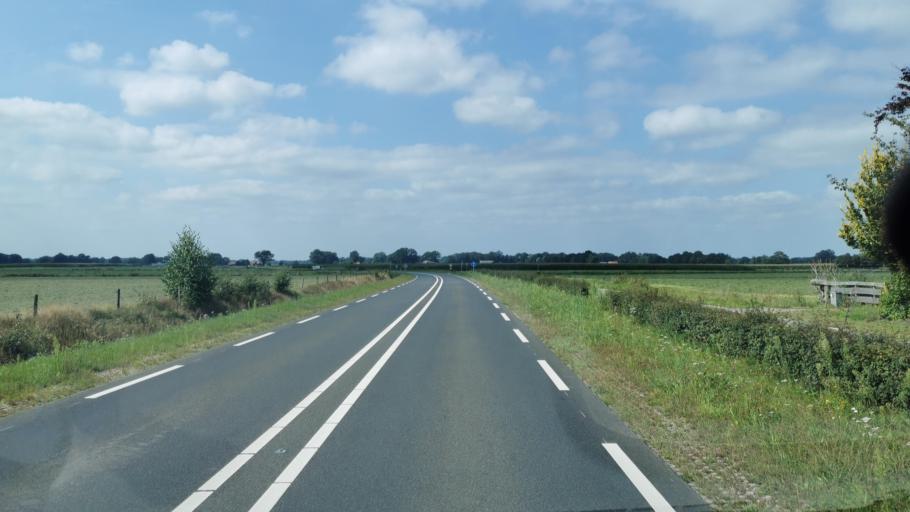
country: NL
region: Overijssel
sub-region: Gemeente Oldenzaal
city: Oldenzaal
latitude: 52.3314
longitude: 6.9091
